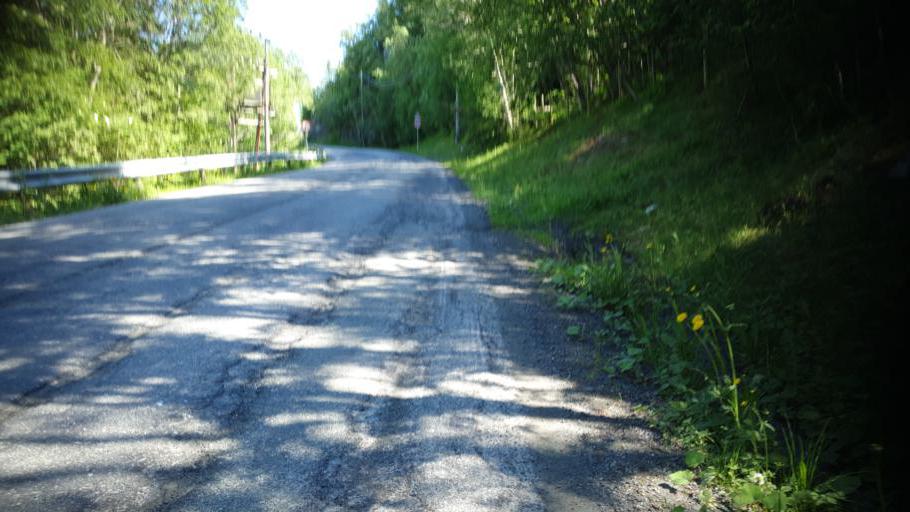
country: NO
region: Sor-Trondelag
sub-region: Malvik
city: Malvik
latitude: 63.4320
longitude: 10.5995
